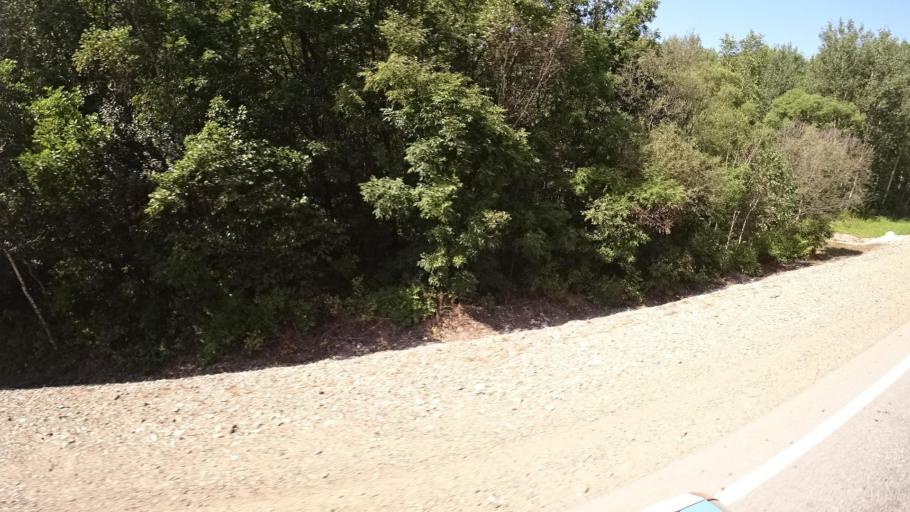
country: RU
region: Khabarovsk Krai
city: Khor
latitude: 47.9787
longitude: 135.0853
